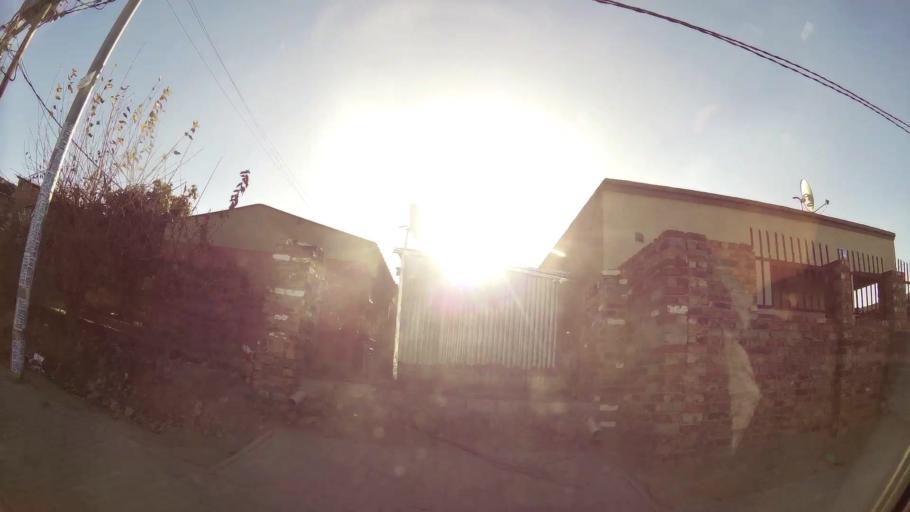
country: ZA
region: Gauteng
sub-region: City of Johannesburg Metropolitan Municipality
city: Diepsloot
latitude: -25.9296
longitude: 28.0055
